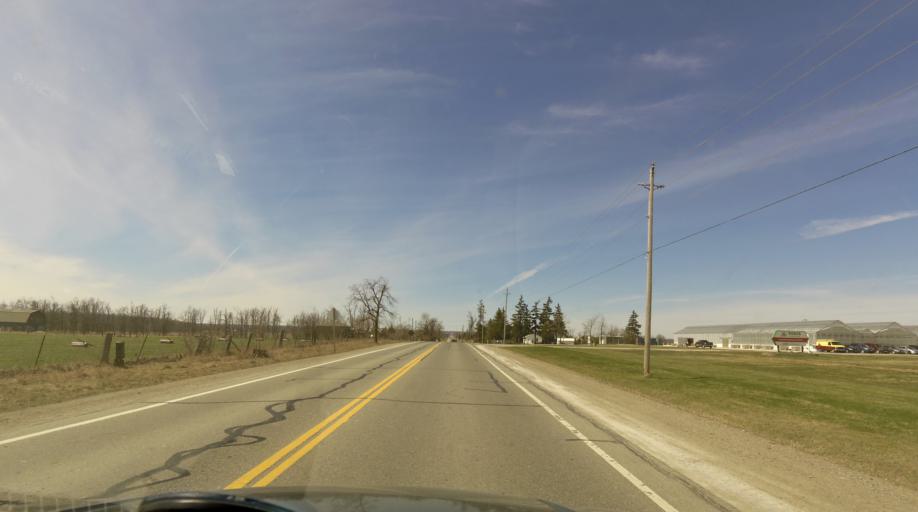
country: CA
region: Ontario
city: Brampton
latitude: 43.6958
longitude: -79.8688
